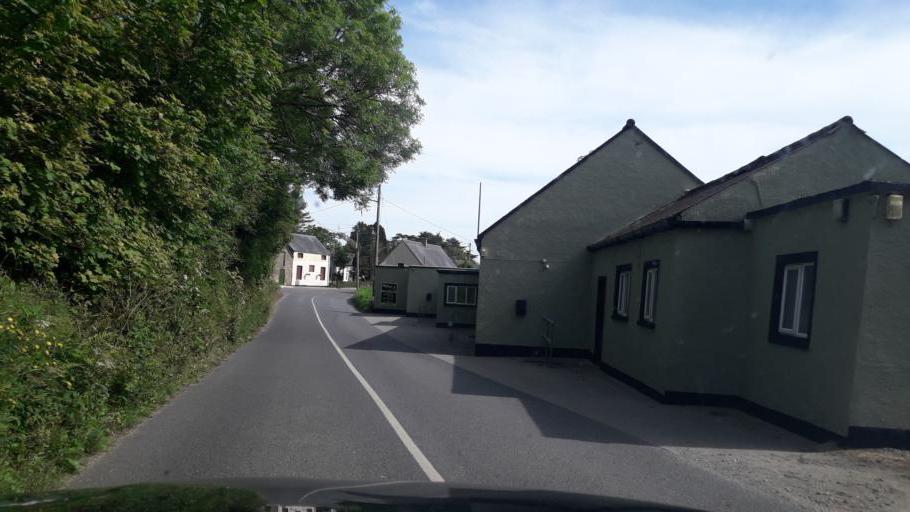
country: IE
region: Leinster
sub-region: Loch Garman
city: Castlebridge
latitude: 52.4138
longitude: -6.4097
